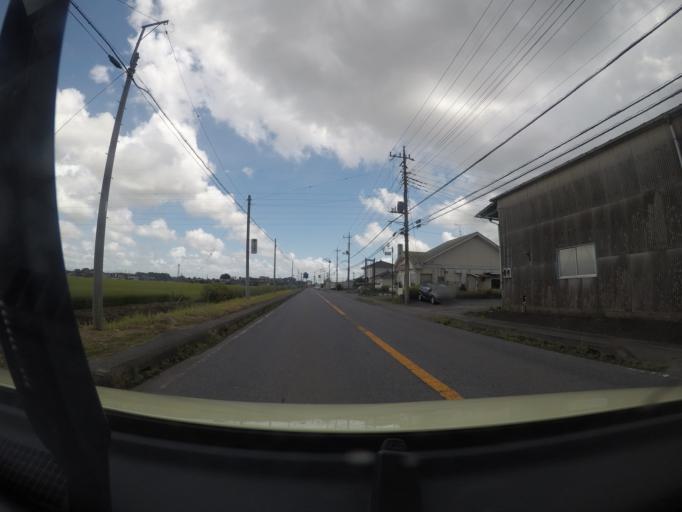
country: JP
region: Ibaraki
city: Mitsukaido
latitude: 36.0259
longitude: 139.9626
